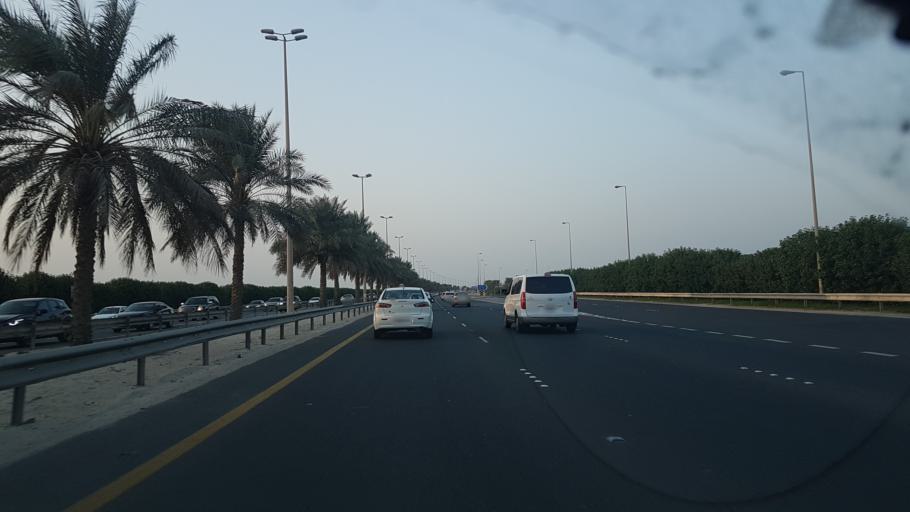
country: BH
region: Northern
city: Madinat `Isa
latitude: 26.1603
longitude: 50.5049
